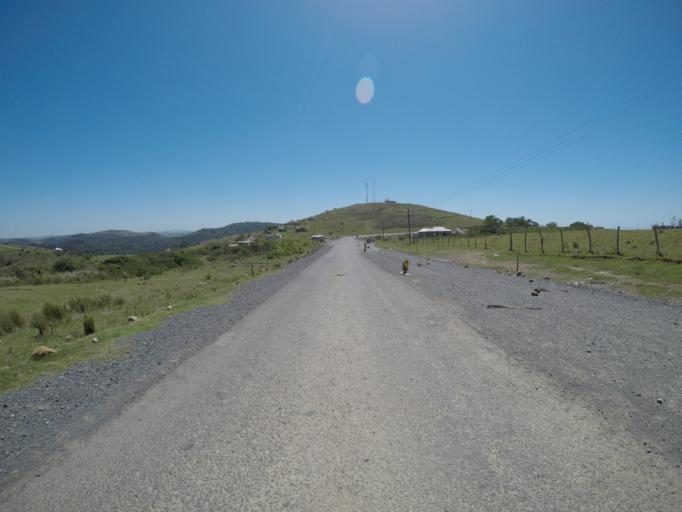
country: ZA
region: Eastern Cape
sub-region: OR Tambo District Municipality
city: Libode
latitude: -32.0021
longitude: 29.1164
